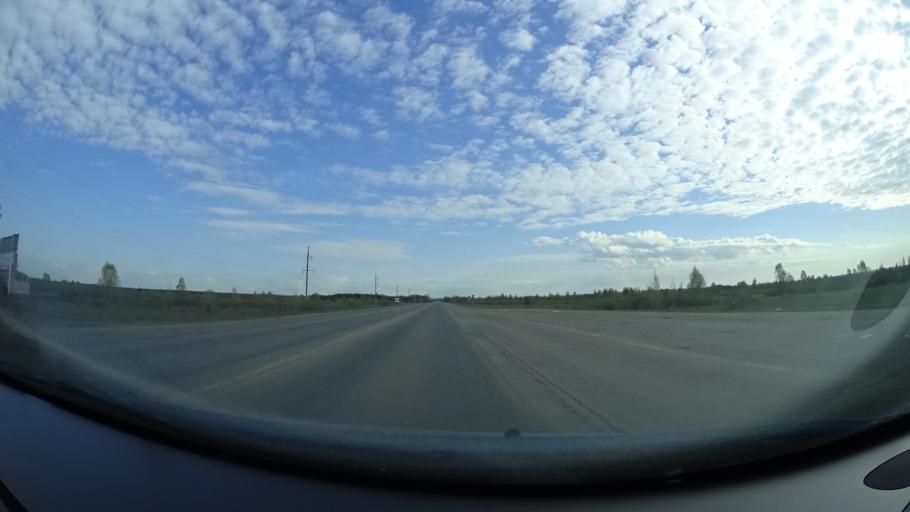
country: RU
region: Bashkortostan
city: Blagoveshchensk
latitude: 54.9892
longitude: 55.7746
